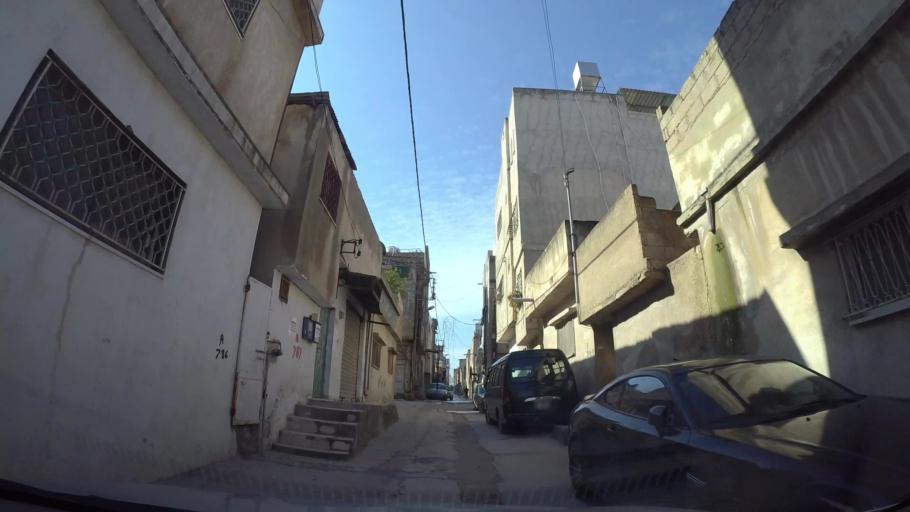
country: JO
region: Amman
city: Al Jubayhah
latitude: 32.0743
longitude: 35.8416
